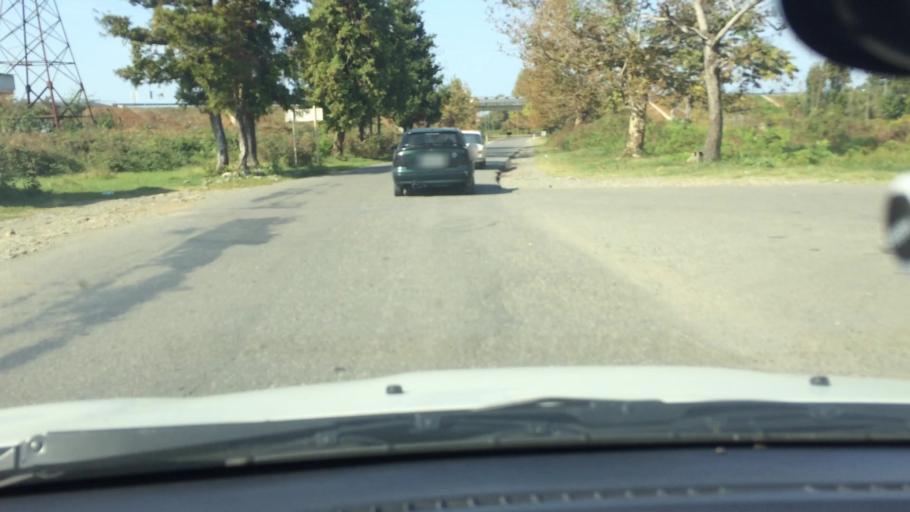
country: GE
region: Ajaria
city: Kobuleti
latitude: 41.8055
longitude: 41.7972
